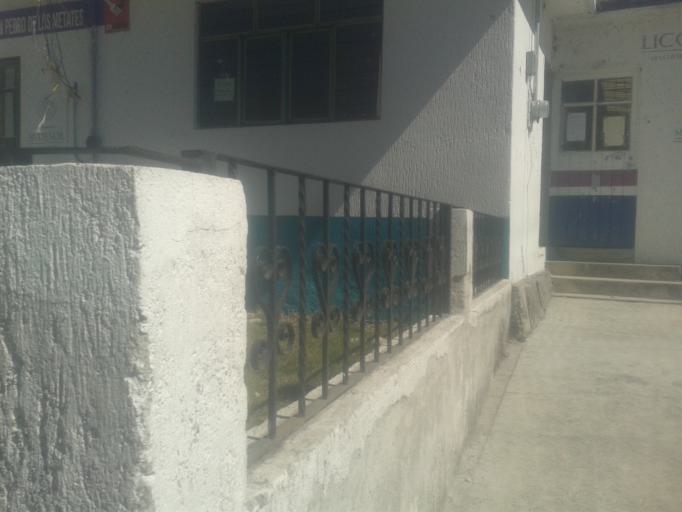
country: MX
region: Mexico
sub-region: Atlacomulco
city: San Bartolo Lanzados
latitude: 19.8975
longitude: -99.8590
